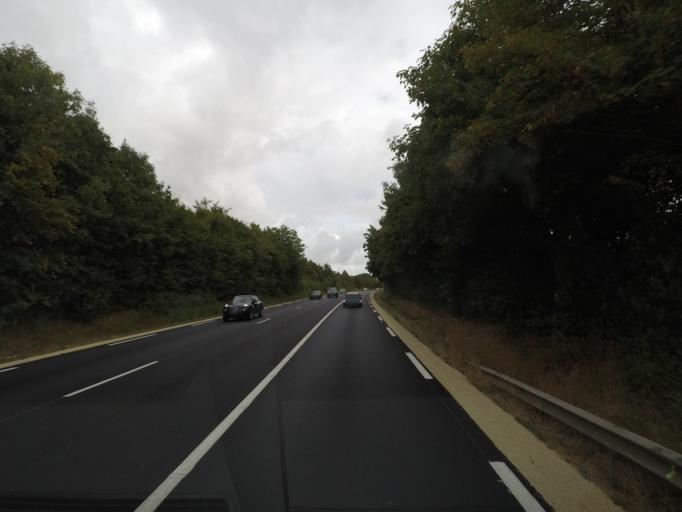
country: FR
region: Poitou-Charentes
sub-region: Departement des Deux-Sevres
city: Celles-sur-Belle
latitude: 46.2636
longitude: -0.2277
